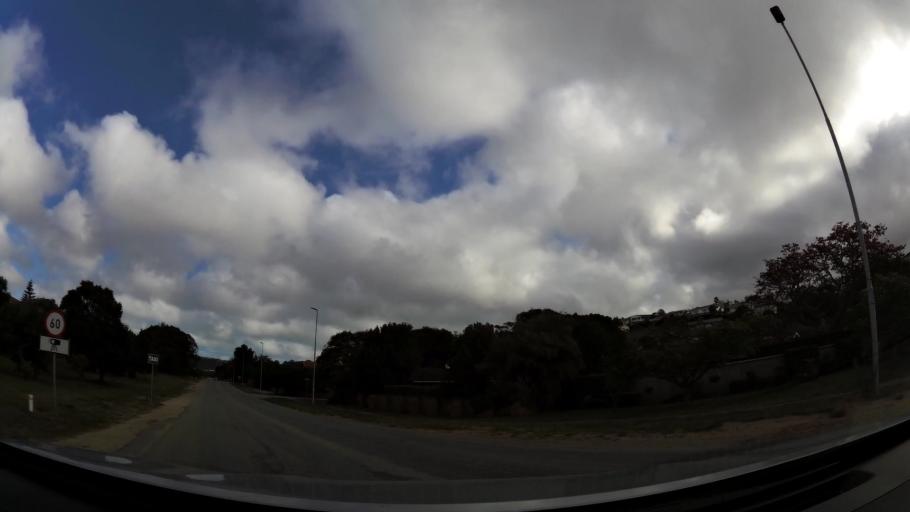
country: ZA
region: Western Cape
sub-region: Eden District Municipality
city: Plettenberg Bay
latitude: -34.0695
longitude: 23.3691
